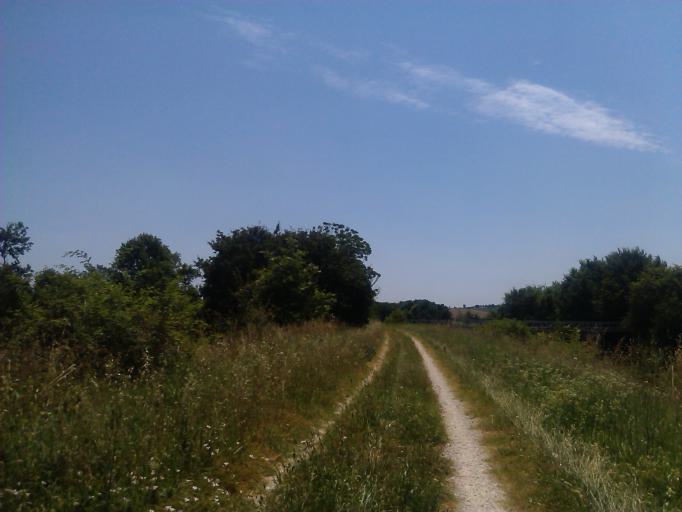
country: IT
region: Tuscany
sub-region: Province of Arezzo
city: Cesa
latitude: 43.3150
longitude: 11.8389
